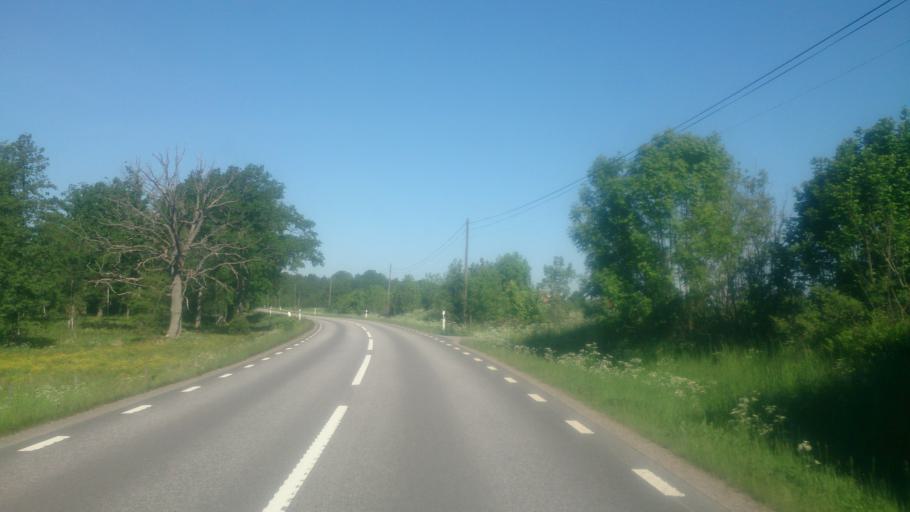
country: SE
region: OEstergoetland
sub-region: Atvidabergs Kommun
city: Atvidaberg
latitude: 58.1393
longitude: 16.0875
